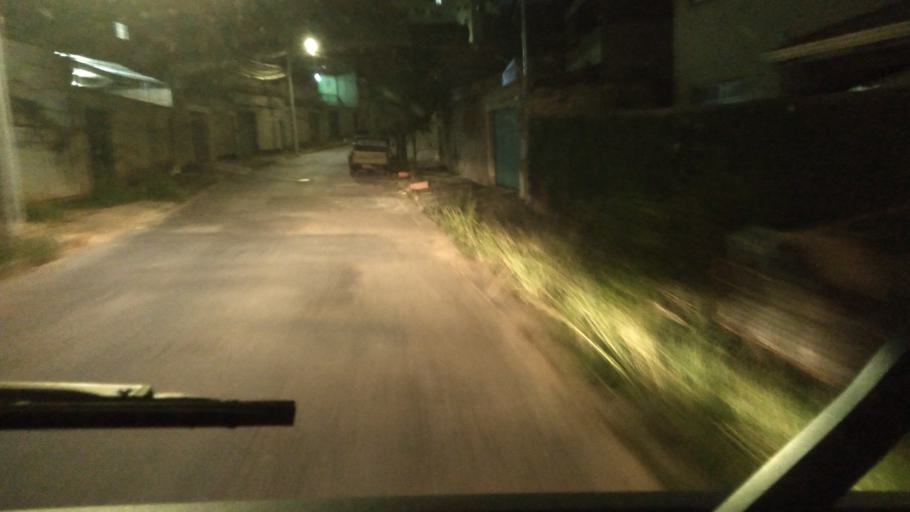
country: BR
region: Minas Gerais
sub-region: Belo Horizonte
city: Belo Horizonte
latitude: -19.8732
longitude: -43.9482
